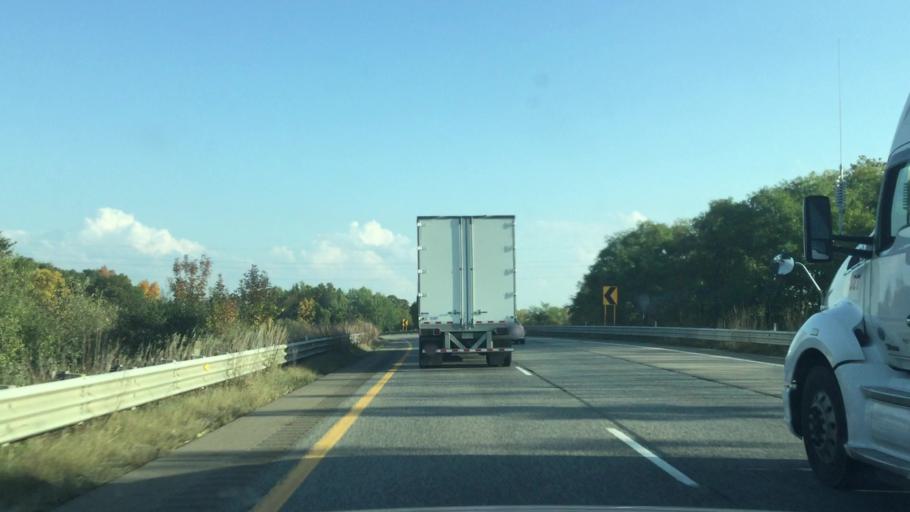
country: US
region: Michigan
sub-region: Washtenaw County
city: Chelsea
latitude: 42.2940
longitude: -84.0889
